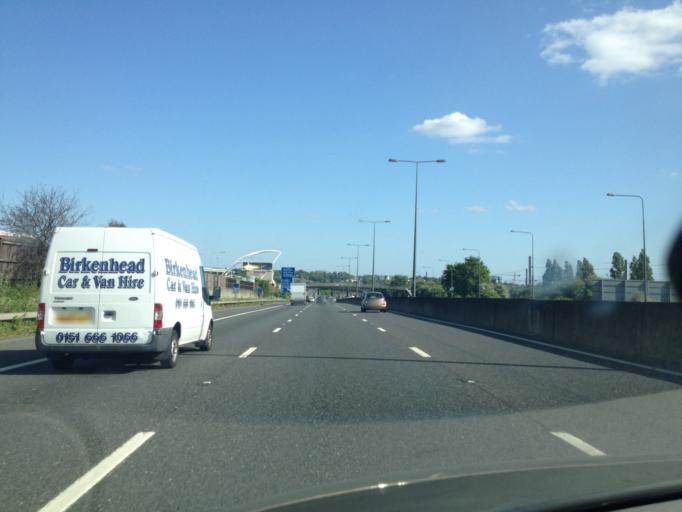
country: GB
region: England
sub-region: Greater London
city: Hendon
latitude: 51.6069
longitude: -0.2424
